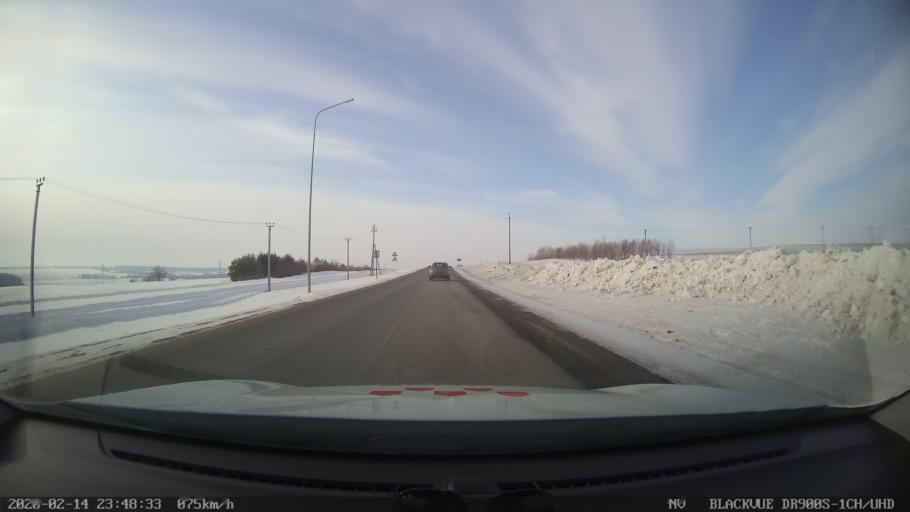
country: RU
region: Tatarstan
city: Kuybyshevskiy Zaton
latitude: 55.2484
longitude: 49.2007
